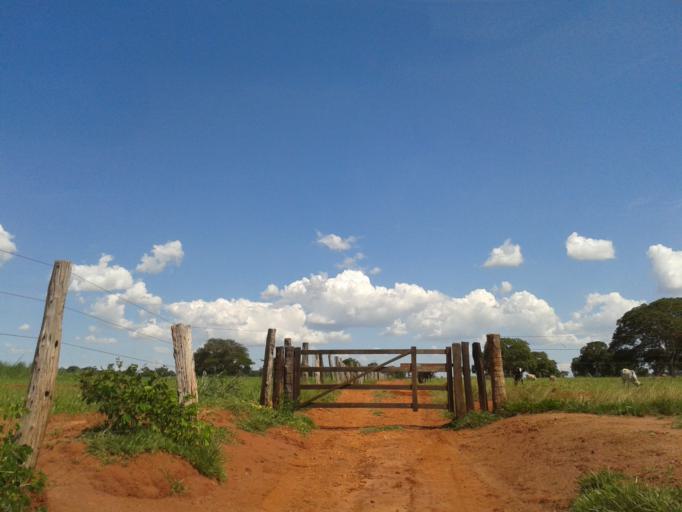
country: BR
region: Minas Gerais
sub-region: Santa Vitoria
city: Santa Vitoria
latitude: -19.1341
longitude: -50.5464
